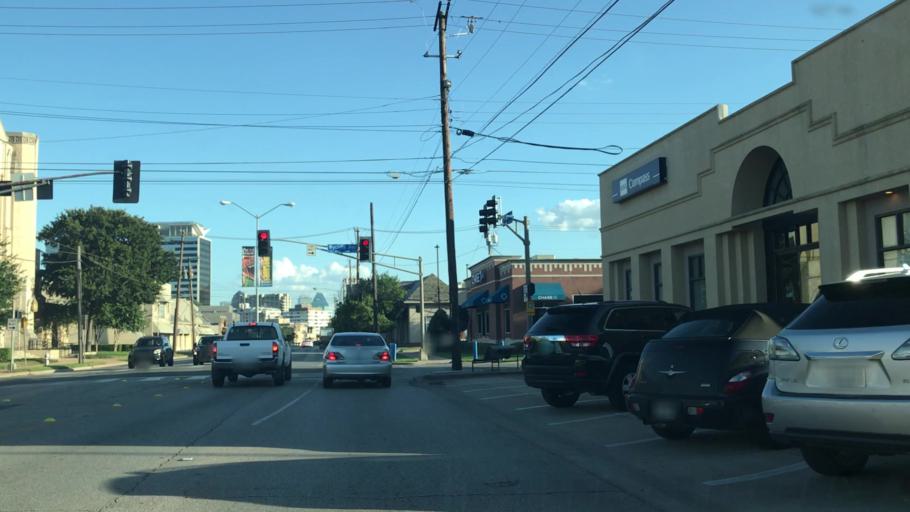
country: US
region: Texas
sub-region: Dallas County
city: Highland Park
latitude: 32.8200
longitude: -96.8024
